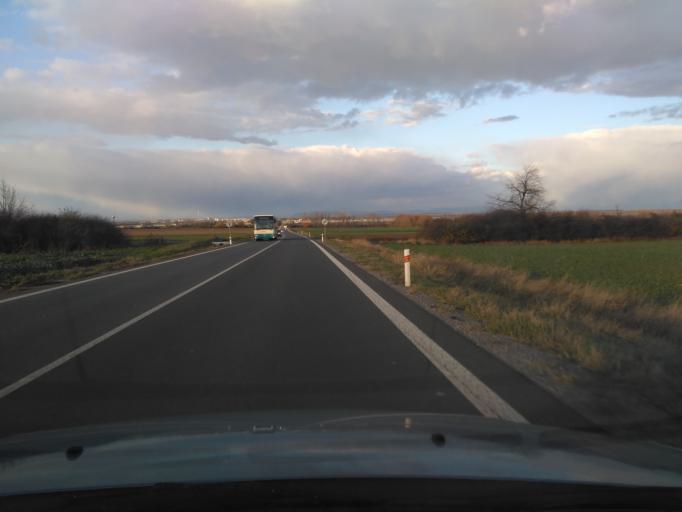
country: SK
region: Kosicky
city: Trebisov
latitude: 48.5782
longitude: 21.7055
